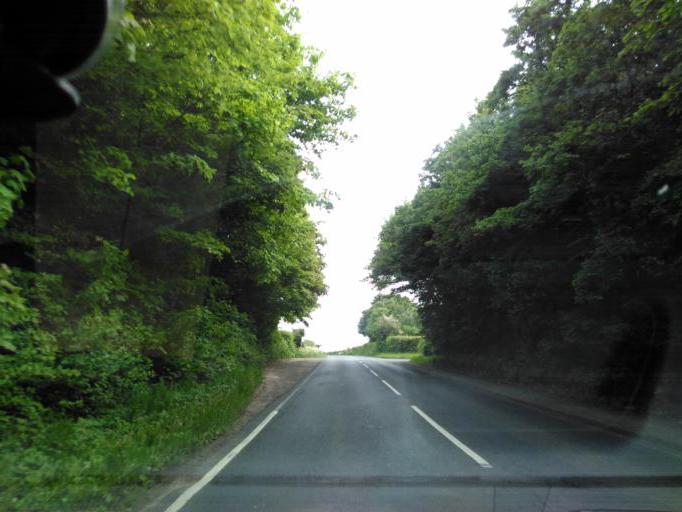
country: GB
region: England
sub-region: Kent
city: Canterbury
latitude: 51.2445
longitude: 1.0795
